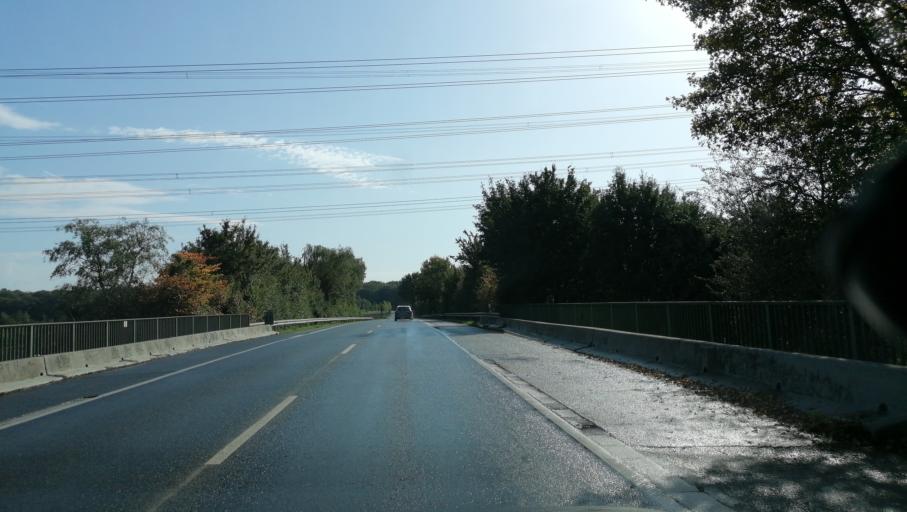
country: DE
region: North Rhine-Westphalia
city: Datteln
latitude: 51.6313
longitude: 7.3494
